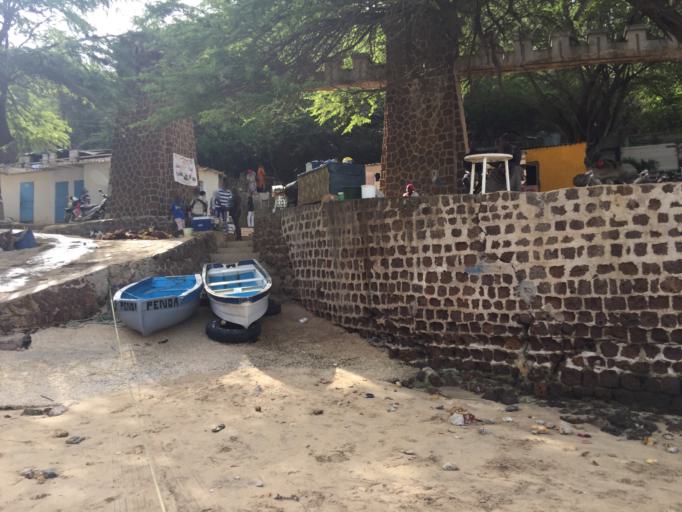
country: SN
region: Dakar
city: Dakar
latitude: 14.6597
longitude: -17.4343
